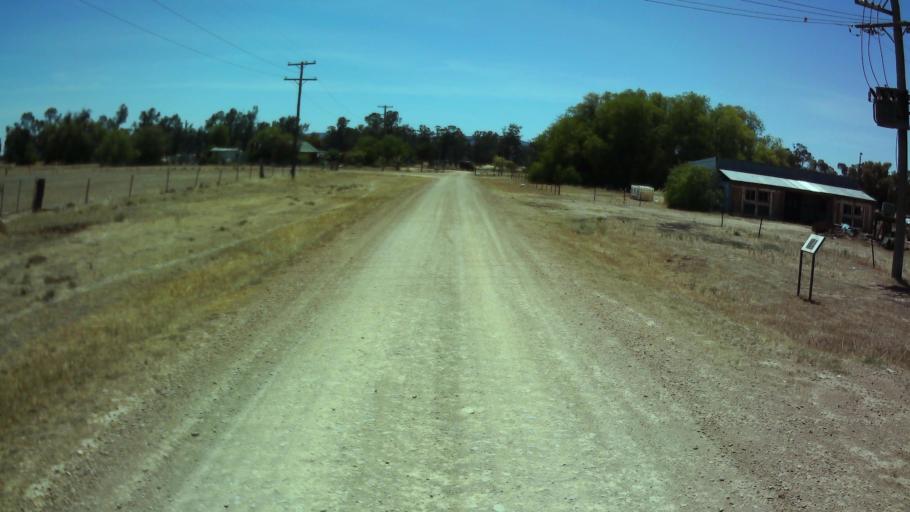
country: AU
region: New South Wales
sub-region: Weddin
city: Grenfell
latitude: -34.0372
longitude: 147.9303
